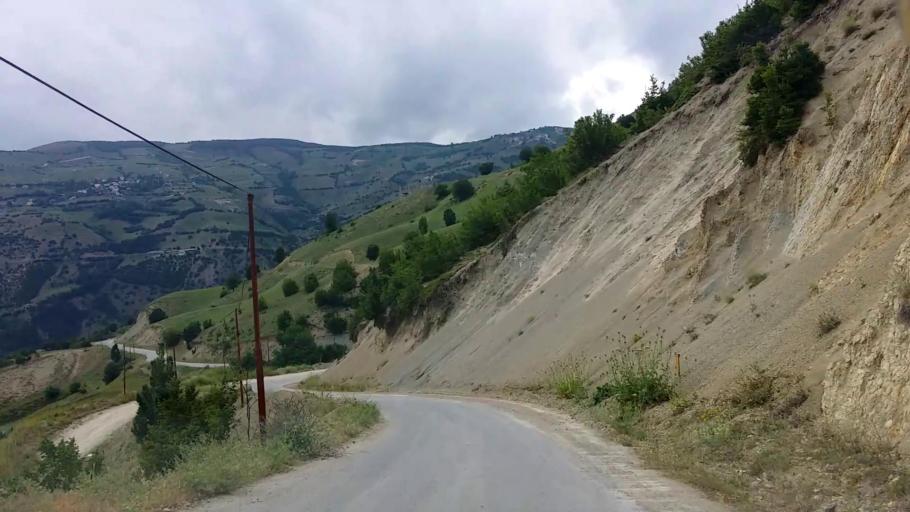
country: IR
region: Mazandaran
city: Chalus
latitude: 36.5532
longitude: 51.2881
